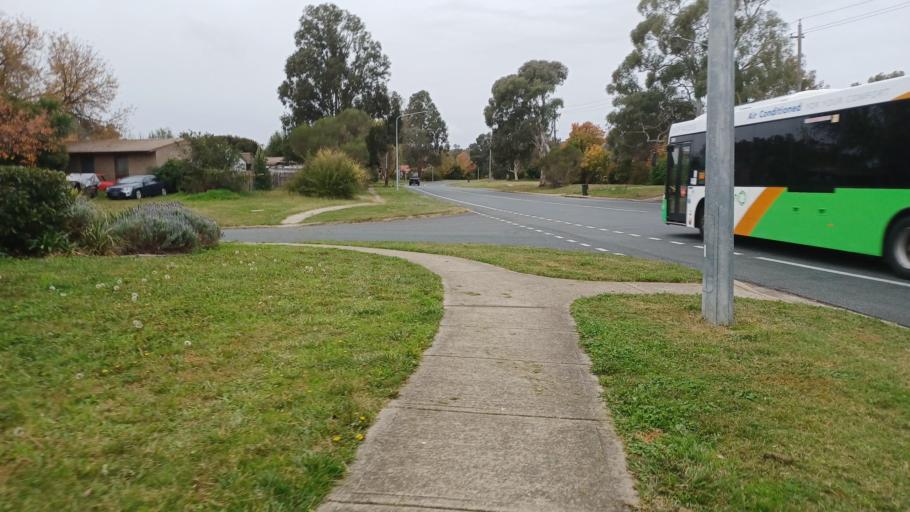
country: AU
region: Australian Capital Territory
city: Belconnen
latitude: -35.2041
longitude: 149.0390
